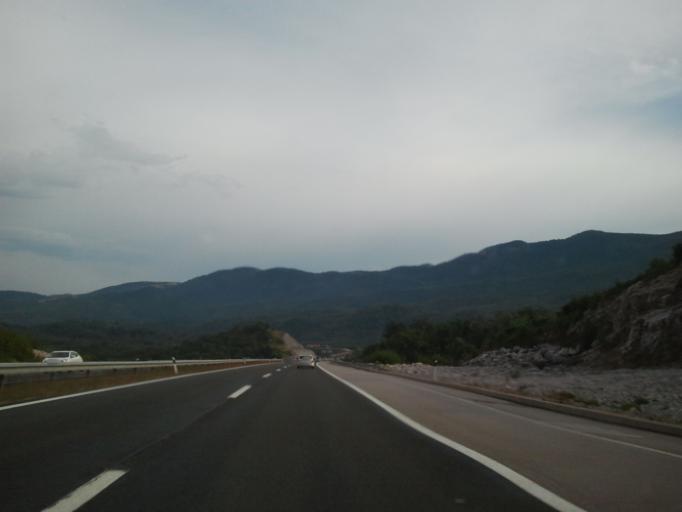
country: HR
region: Zadarska
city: Obrovac
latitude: 44.3172
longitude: 15.6769
